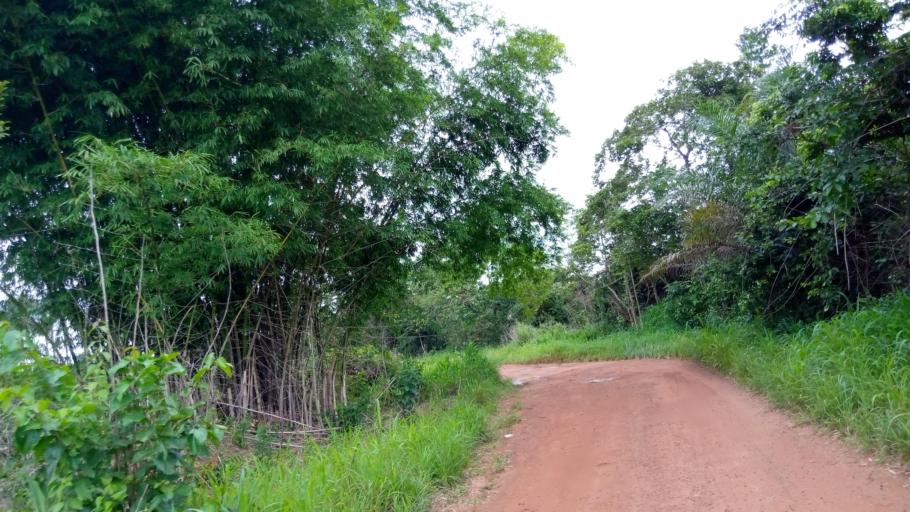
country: SL
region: Southern Province
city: Moyamba
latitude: 8.1958
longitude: -12.5458
